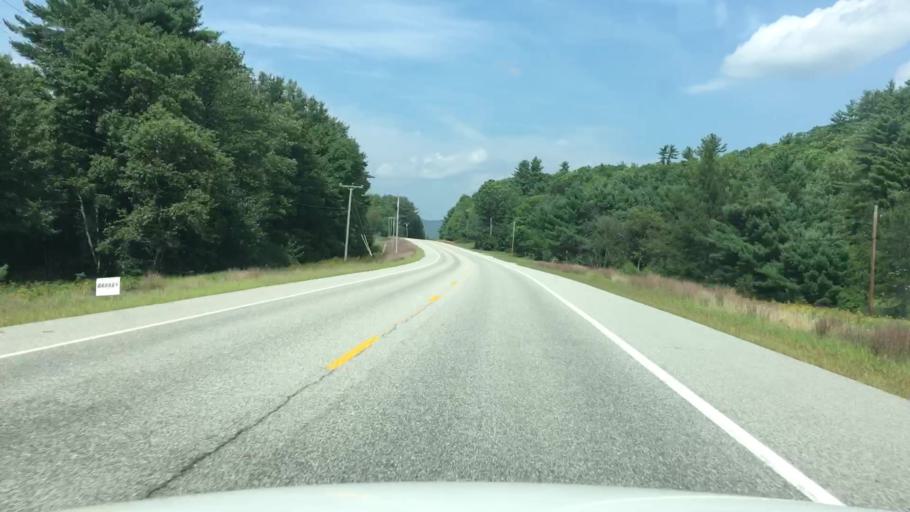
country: US
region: Maine
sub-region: Oxford County
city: Canton
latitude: 44.4547
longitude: -70.3181
